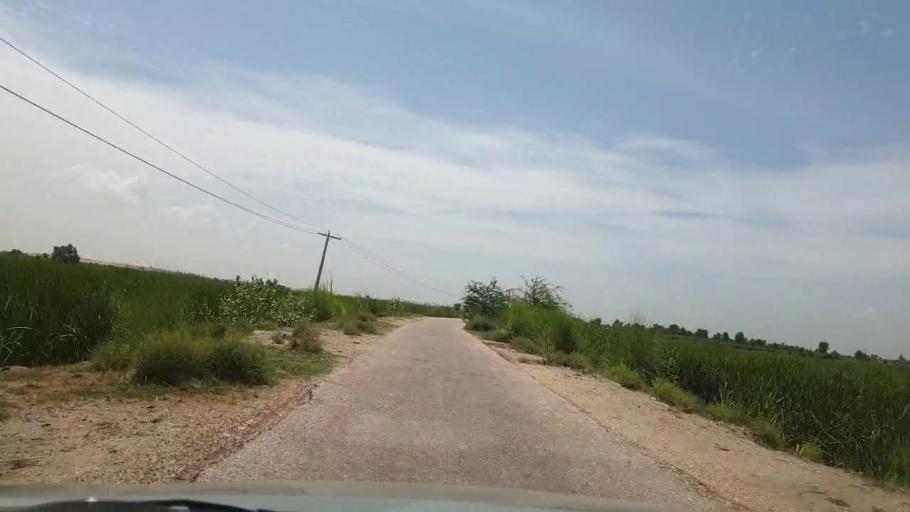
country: PK
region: Sindh
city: Bozdar
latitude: 27.0610
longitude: 68.9823
